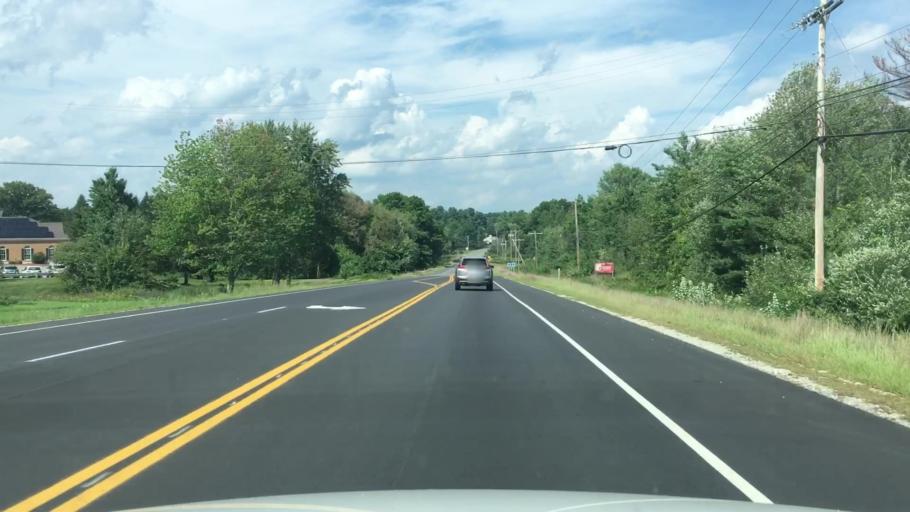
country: US
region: New Hampshire
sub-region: Rockingham County
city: Londonderry
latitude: 42.8520
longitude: -71.3573
